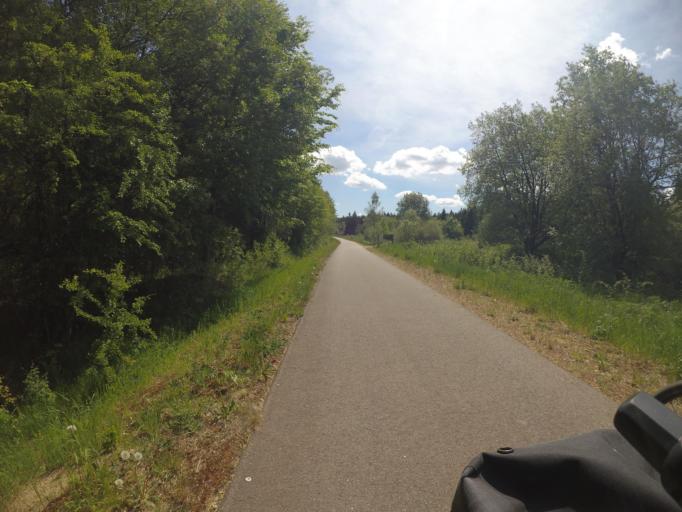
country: BE
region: Wallonia
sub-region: Province de Liege
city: Bullange
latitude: 50.3747
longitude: 6.3194
